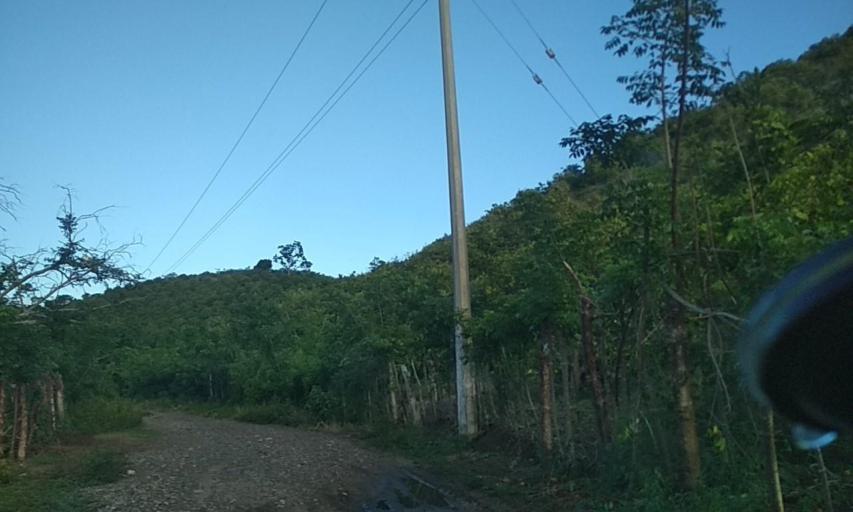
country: MX
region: Veracruz
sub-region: Papantla
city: Polutla
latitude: 20.5585
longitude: -97.2321
